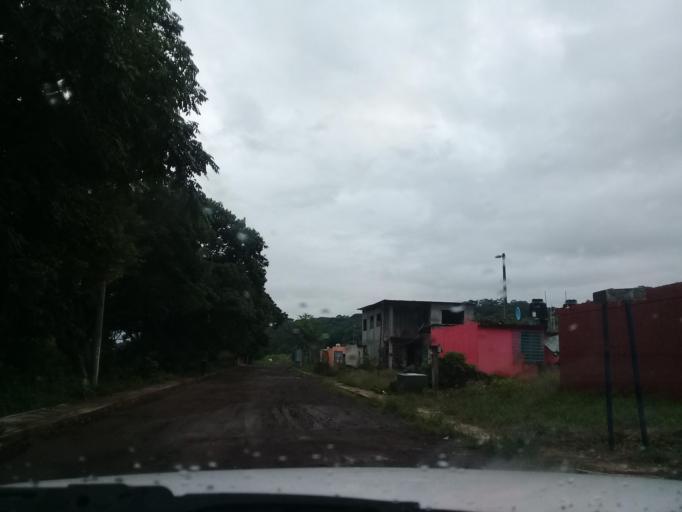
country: MX
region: Veracruz
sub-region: San Andres Tuxtla
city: Texalpan de Arriba
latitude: 18.4257
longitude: -95.2215
